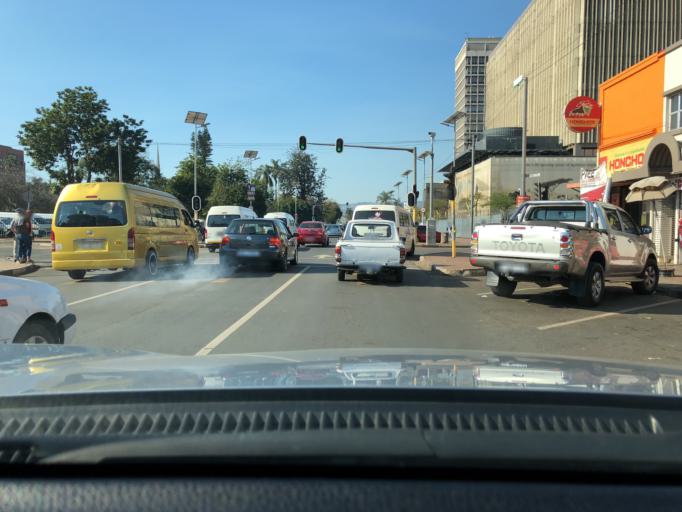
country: ZA
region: KwaZulu-Natal
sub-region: uMgungundlovu District Municipality
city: Pietermaritzburg
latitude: -29.6018
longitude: 30.3812
